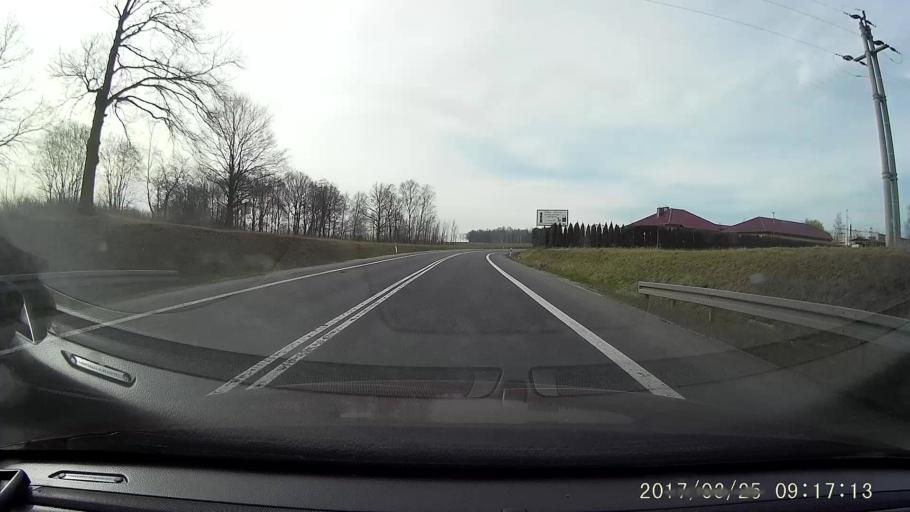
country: PL
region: Lower Silesian Voivodeship
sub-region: Powiat zgorzelecki
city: Zgorzelec
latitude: 51.1298
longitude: 15.0216
